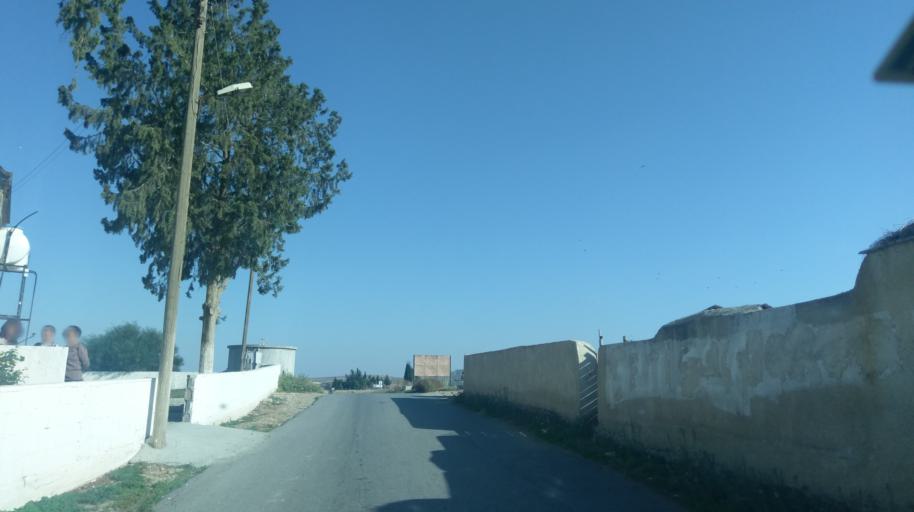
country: CY
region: Larnaka
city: Troulloi
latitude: 35.0832
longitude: 33.6098
